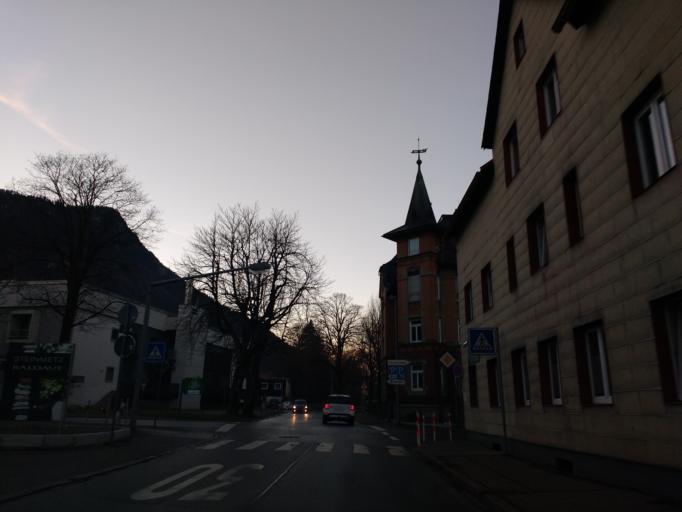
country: DE
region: Bavaria
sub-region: Swabia
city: Immenstadt im Allgau
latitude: 47.5617
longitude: 10.2183
